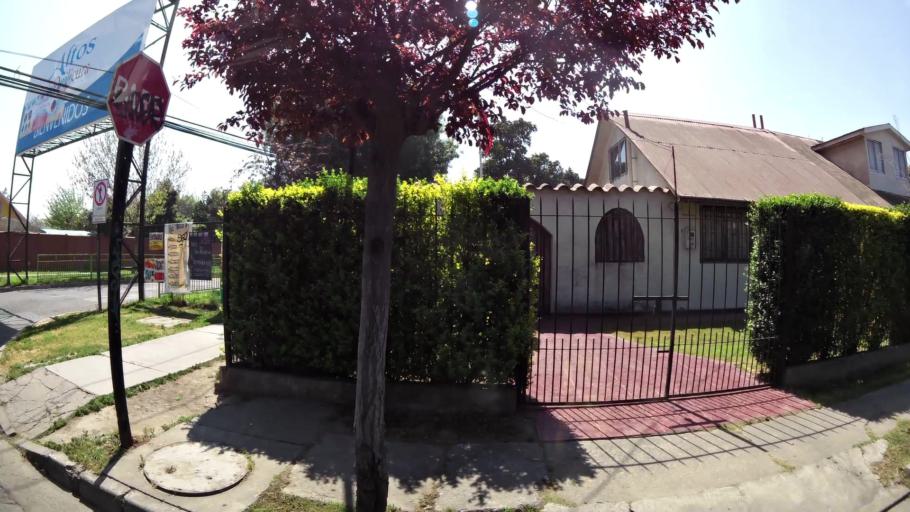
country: CL
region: Santiago Metropolitan
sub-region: Provincia de Santiago
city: Lo Prado
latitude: -33.3637
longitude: -70.7138
